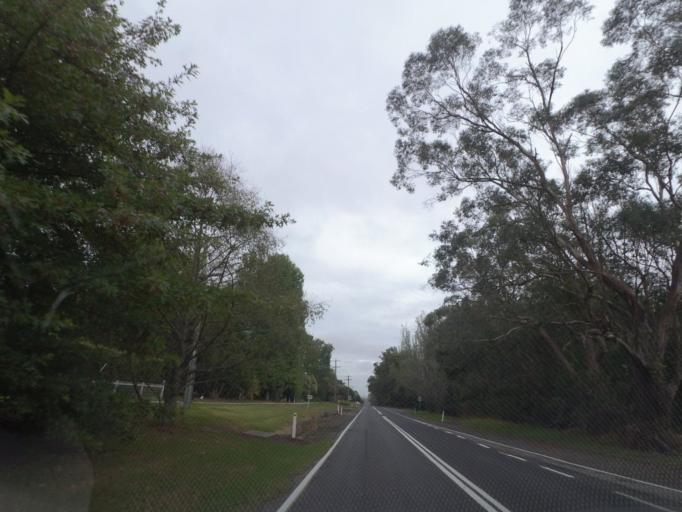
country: AU
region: Victoria
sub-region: Yarra Ranges
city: Healesville
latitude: -37.6638
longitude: 145.5324
